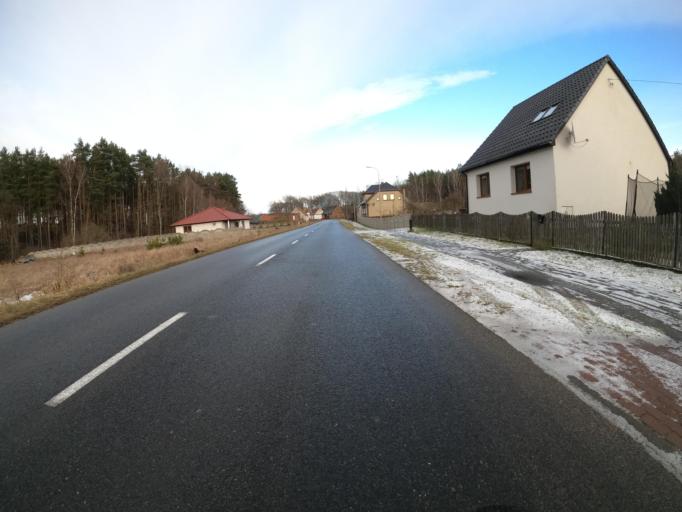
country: PL
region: Lubusz
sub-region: Powiat slubicki
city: Cybinka
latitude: 52.2167
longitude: 14.8404
